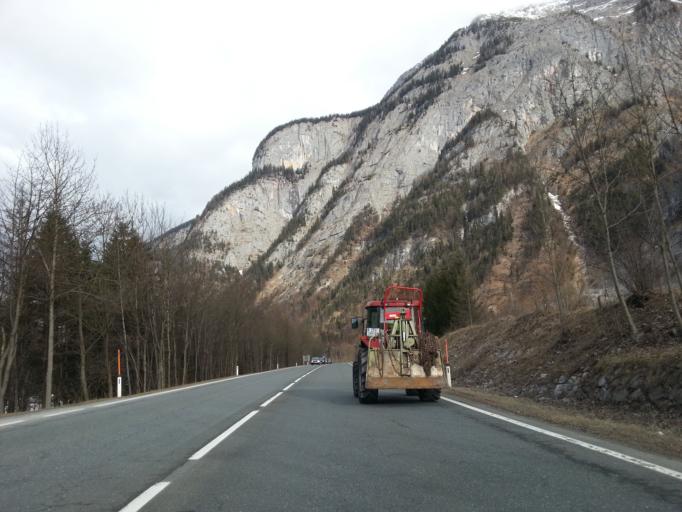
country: AT
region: Salzburg
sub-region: Politischer Bezirk Zell am See
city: Saalfelden am Steinernen Meer
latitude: 47.4841
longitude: 12.8275
